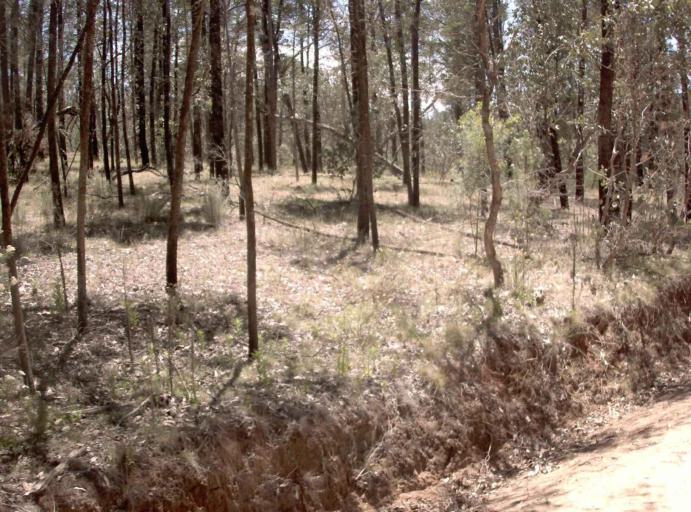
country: AU
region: New South Wales
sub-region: Snowy River
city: Jindabyne
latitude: -36.8975
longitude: 148.4189
